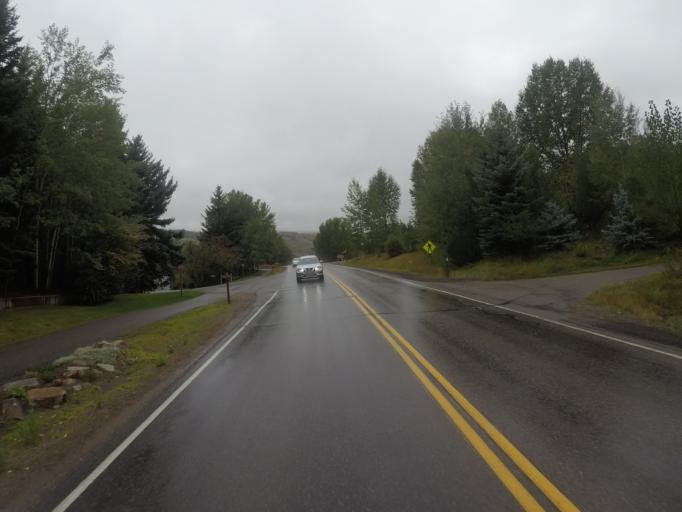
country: US
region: Colorado
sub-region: Pitkin County
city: Snowmass Village
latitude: 39.2178
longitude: -106.9342
